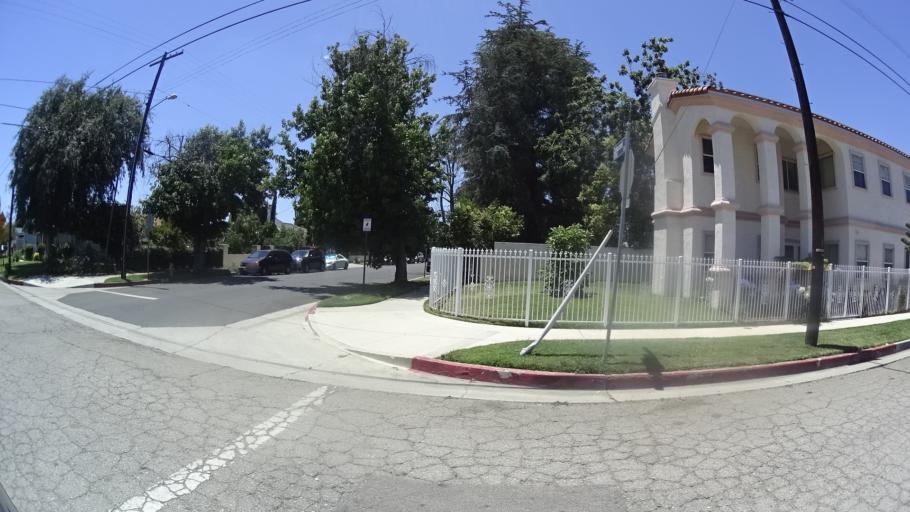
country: US
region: California
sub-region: Los Angeles County
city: Van Nuys
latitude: 34.2067
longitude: -118.4673
